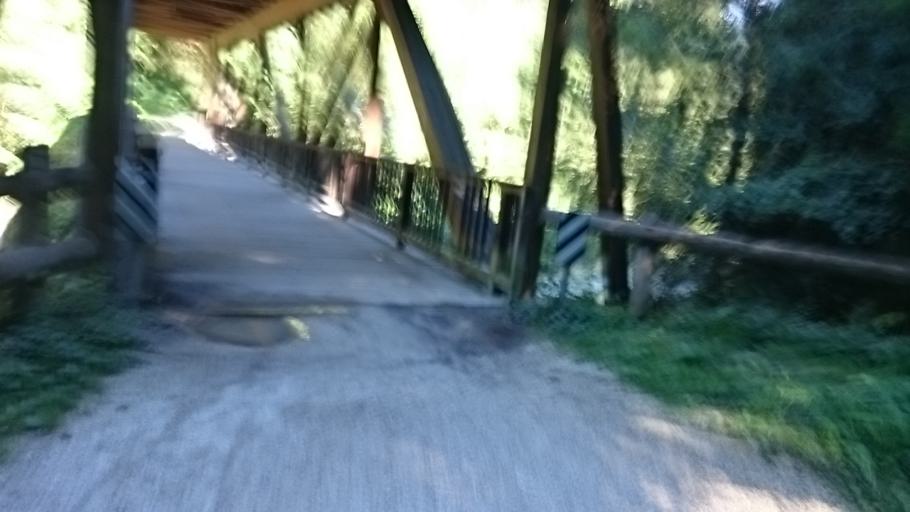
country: IT
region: Trentino-Alto Adige
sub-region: Bolzano
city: Riscone
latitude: 46.7872
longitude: 11.9510
